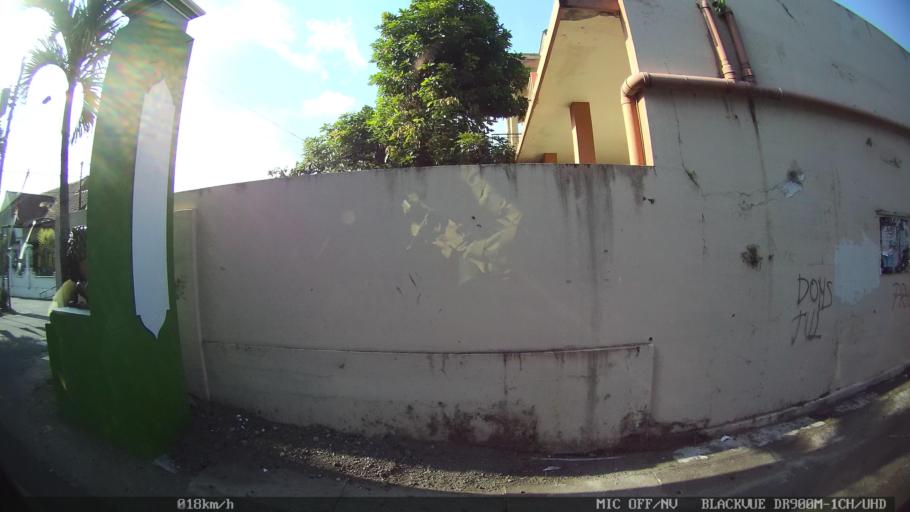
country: ID
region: Daerah Istimewa Yogyakarta
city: Yogyakarta
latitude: -7.8216
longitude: 110.3824
